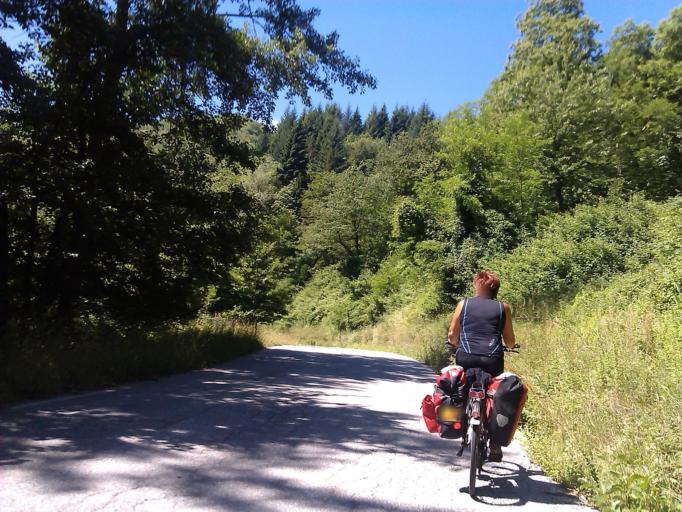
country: IT
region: Tuscany
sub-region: Provincia di Pistoia
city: Sambuca Pistoiese
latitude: 44.0758
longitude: 11.0520
